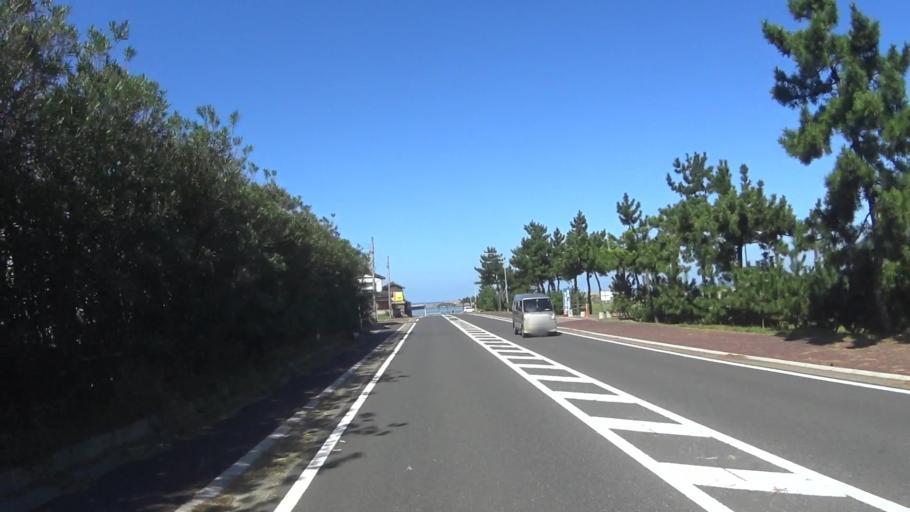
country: JP
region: Kyoto
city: Miyazu
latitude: 35.6899
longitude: 135.0195
